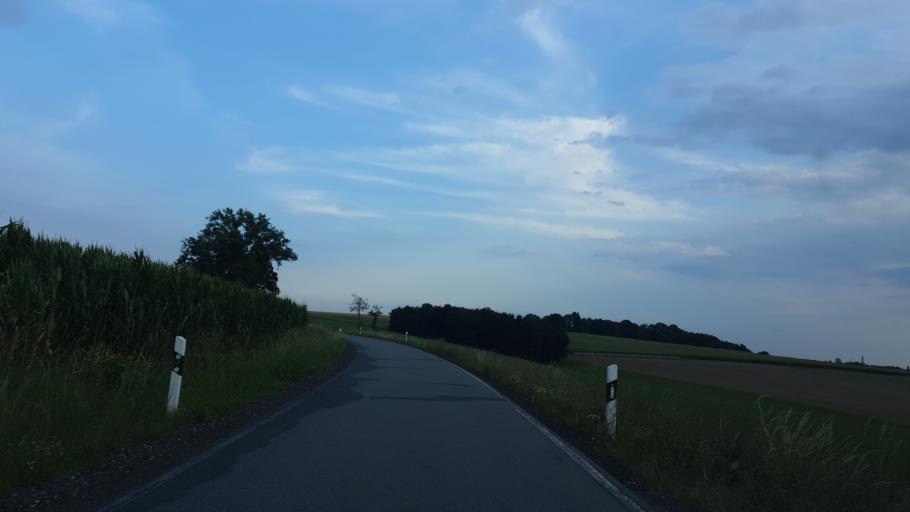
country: DE
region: Saxony
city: Kirchberg
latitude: 50.7542
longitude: 12.7338
